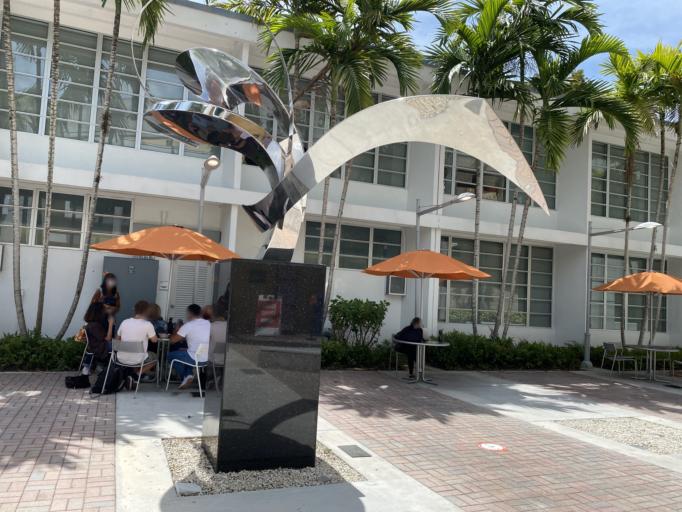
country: US
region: Florida
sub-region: Miami-Dade County
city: Coral Gables
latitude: 25.7189
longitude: -80.2802
